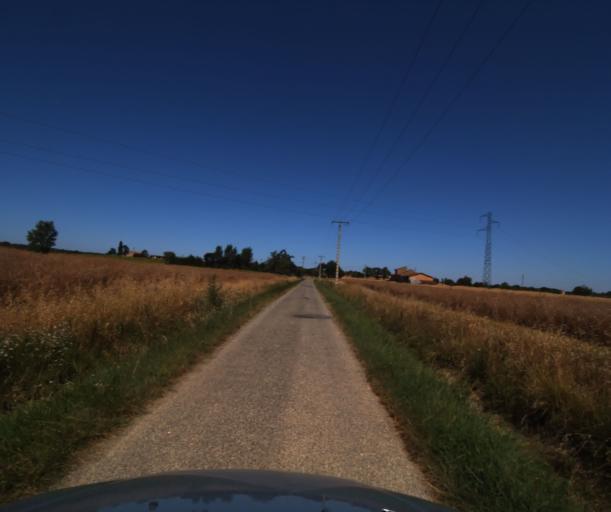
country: FR
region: Midi-Pyrenees
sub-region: Departement de la Haute-Garonne
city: Muret
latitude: 43.4531
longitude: 1.3662
